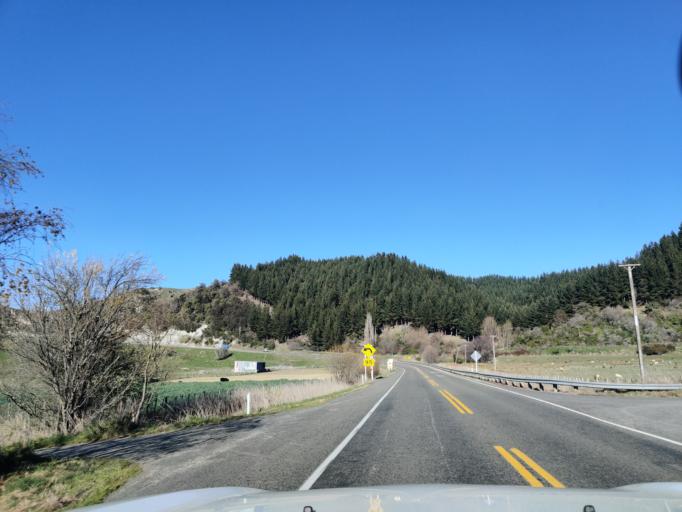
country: NZ
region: Manawatu-Wanganui
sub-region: Ruapehu District
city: Waiouru
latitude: -39.8204
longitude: 175.7779
